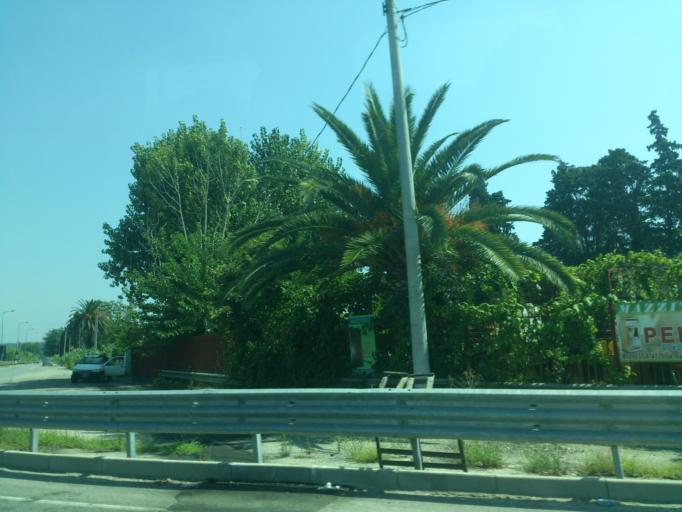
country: IT
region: Calabria
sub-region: Provincia di Reggio Calabria
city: Rosarno
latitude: 38.4664
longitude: 16.0105
